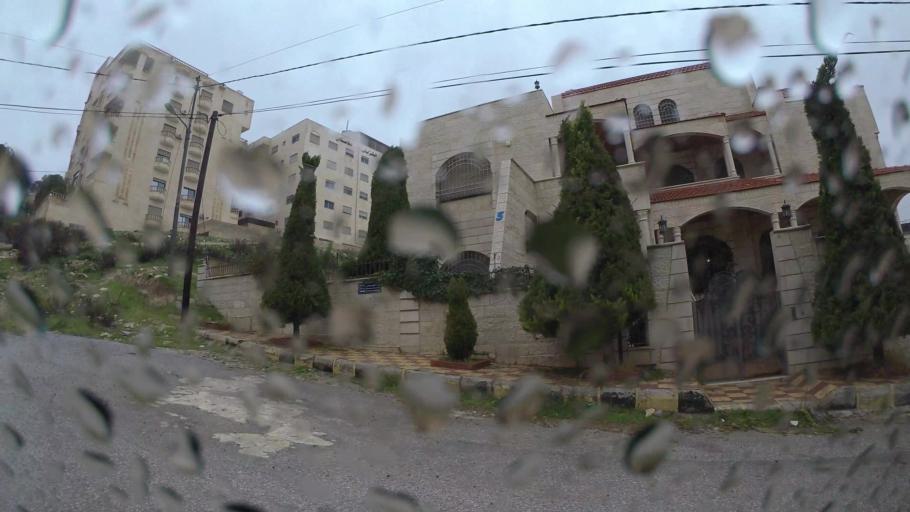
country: JO
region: Amman
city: Al Jubayhah
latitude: 32.0224
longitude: 35.8902
